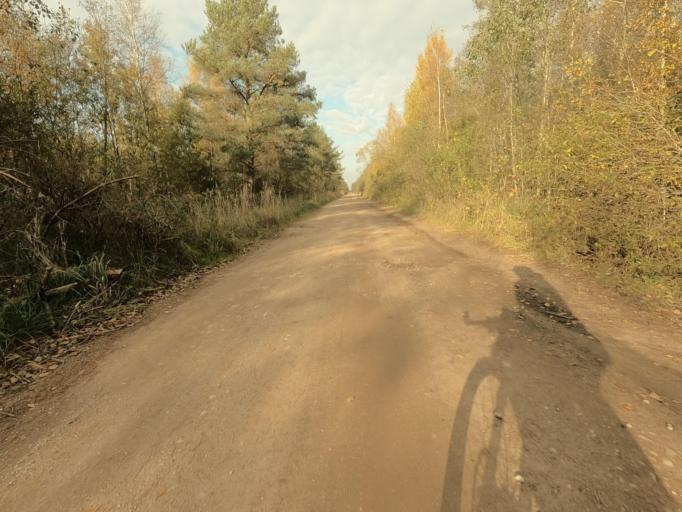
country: RU
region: Novgorod
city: Volkhovskiy
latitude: 58.8951
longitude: 31.0294
